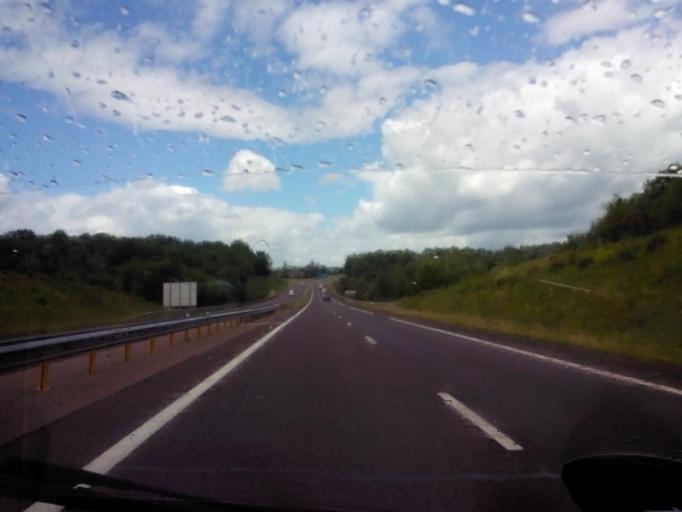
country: FR
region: Lorraine
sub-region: Departement de Meurthe-et-Moselle
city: Dommartin-les-Toul
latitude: 48.6439
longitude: 5.8803
